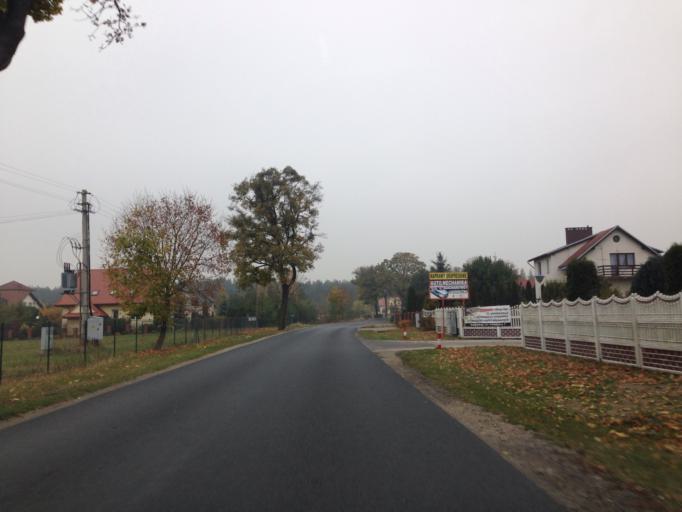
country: PL
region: Kujawsko-Pomorskie
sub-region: Powiat brodnicki
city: Brodnica
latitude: 53.2823
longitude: 19.3867
